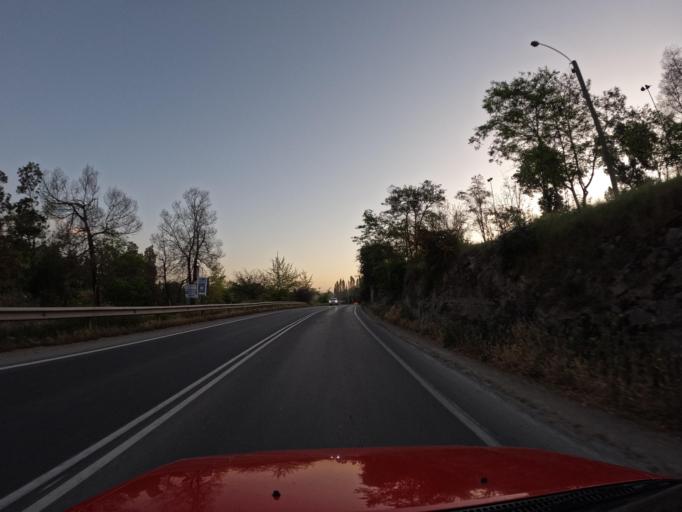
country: CL
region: O'Higgins
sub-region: Provincia de Cachapoal
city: San Vicente
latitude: -34.1778
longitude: -71.3987
